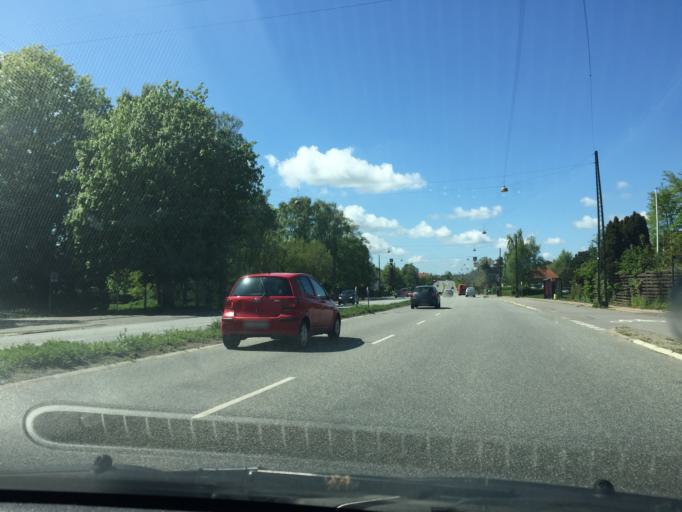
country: DK
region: Capital Region
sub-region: Kobenhavn
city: Vanlose
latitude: 55.6912
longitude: 12.4728
